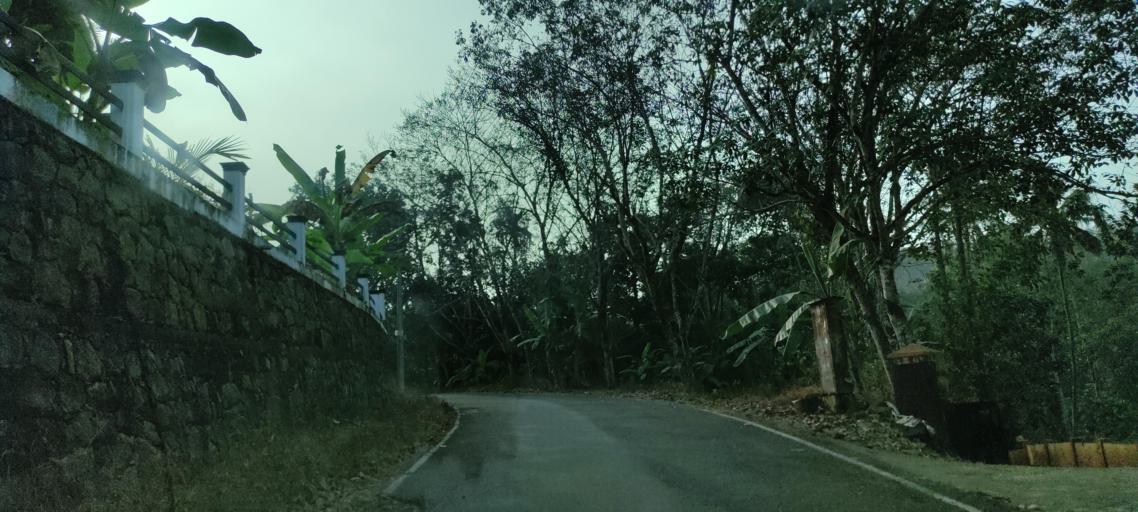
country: IN
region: Kerala
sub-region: Ernakulam
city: Piravam
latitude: 9.8022
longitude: 76.5101
